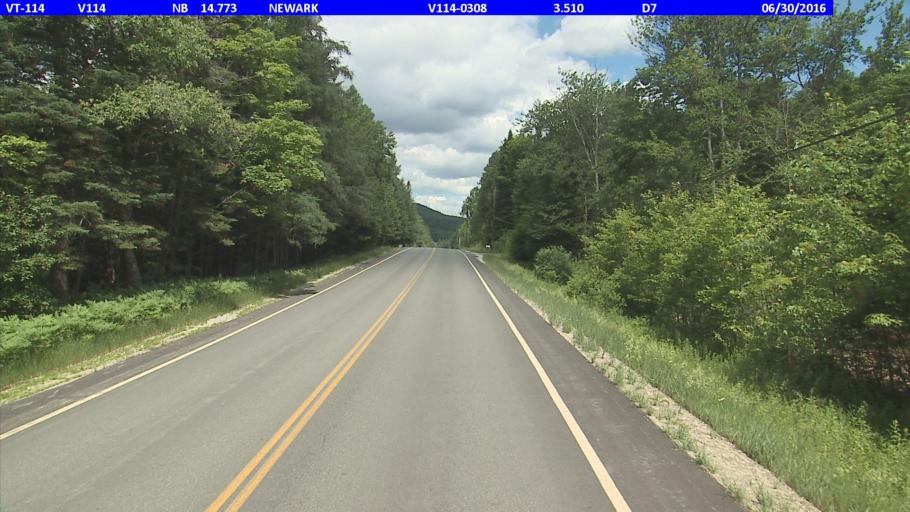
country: US
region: Vermont
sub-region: Caledonia County
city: Lyndonville
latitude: 44.7173
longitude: -71.8690
